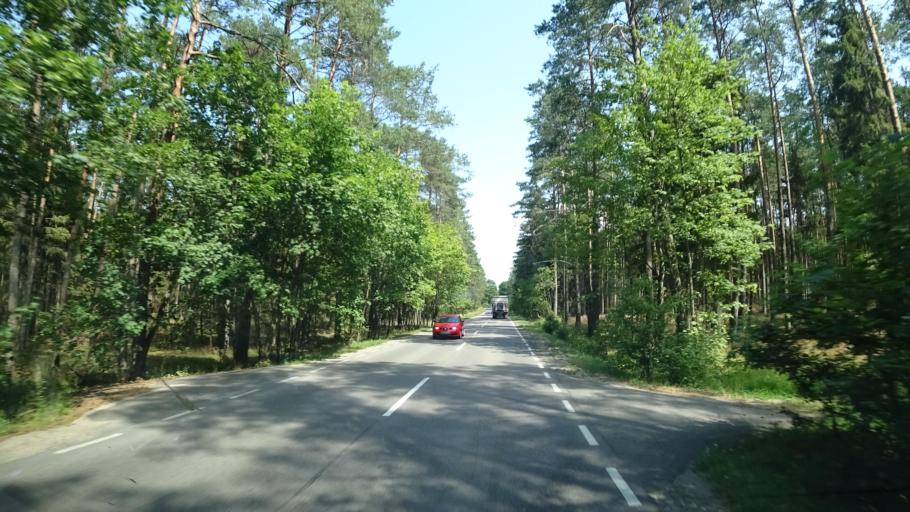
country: PL
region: Pomeranian Voivodeship
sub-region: Powiat koscierski
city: Lipusz
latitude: 54.1201
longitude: 17.8446
